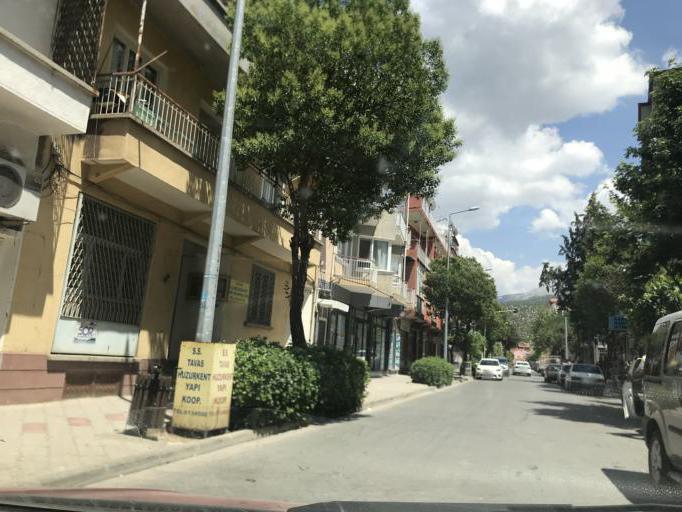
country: TR
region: Denizli
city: Tavas
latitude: 37.5729
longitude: 29.0714
